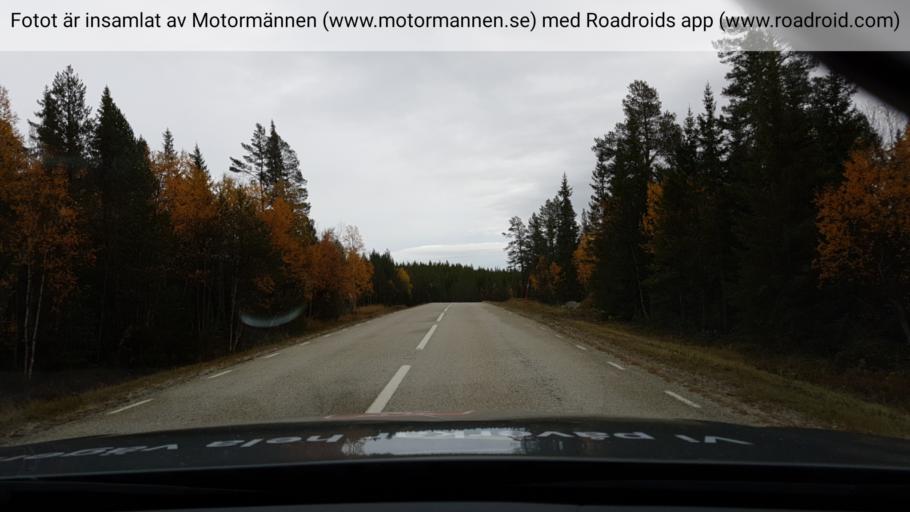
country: SE
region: Jaemtland
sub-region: Are Kommun
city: Are
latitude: 62.8237
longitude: 12.9195
